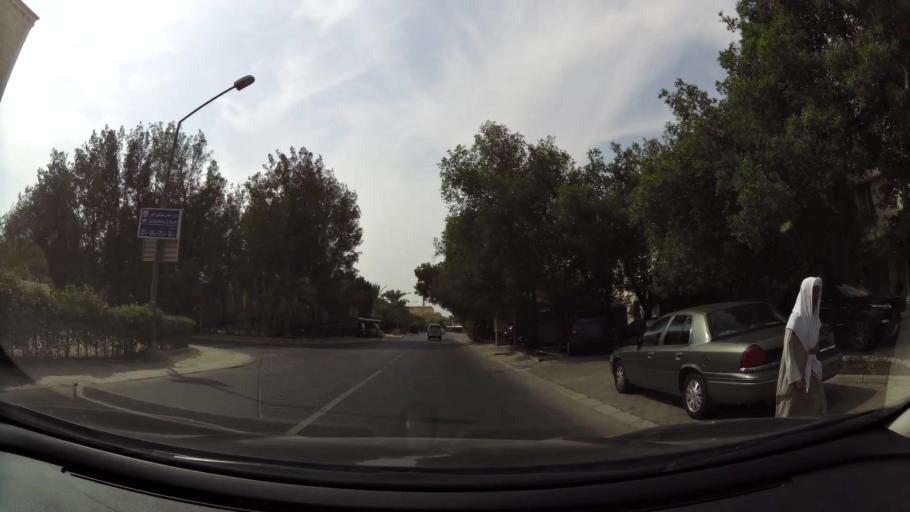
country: KW
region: Al Asimah
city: Ad Dasmah
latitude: 29.3453
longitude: 47.9882
